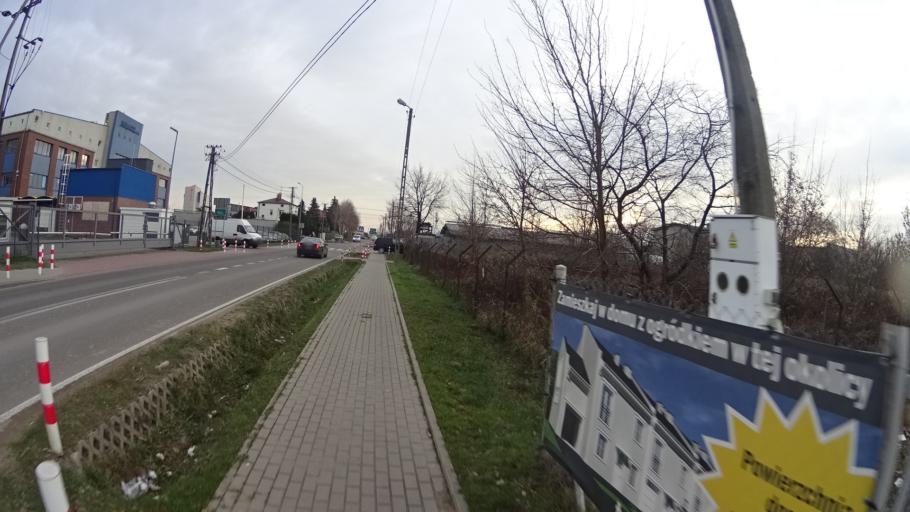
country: PL
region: Masovian Voivodeship
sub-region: Warszawa
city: Ursus
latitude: 52.2179
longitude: 20.8597
